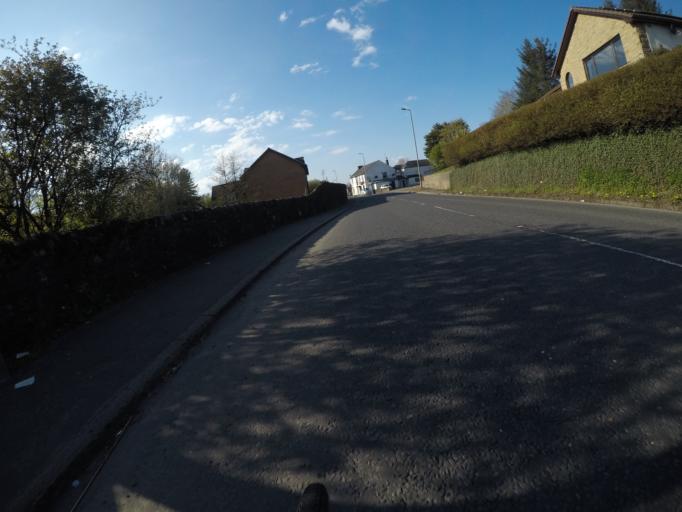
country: GB
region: Scotland
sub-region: North Ayrshire
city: Kilwinning
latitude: 55.6525
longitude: -4.6918
